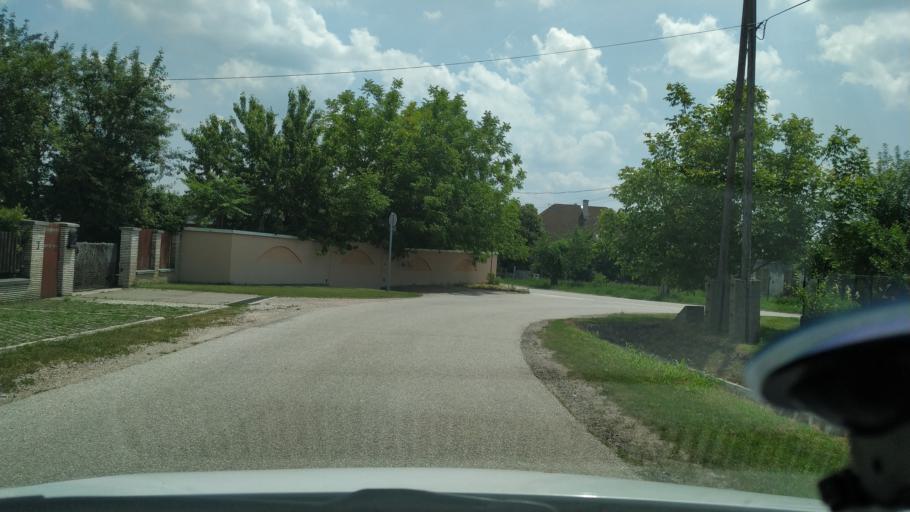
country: HU
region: Veszprem
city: Varpalota
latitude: 47.2001
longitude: 18.1810
